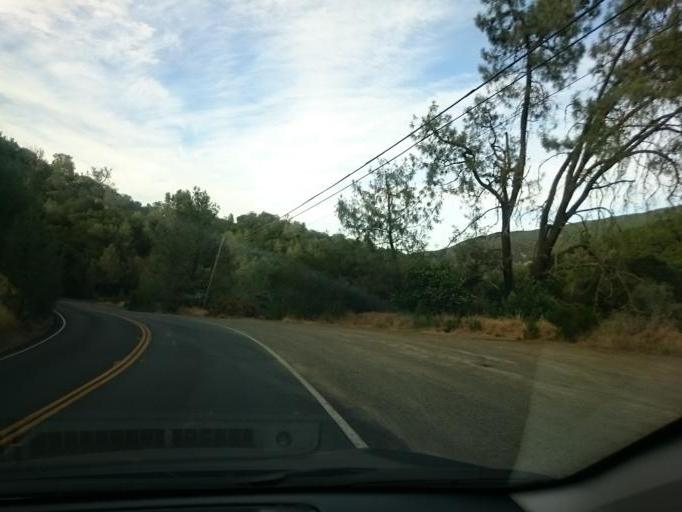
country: US
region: California
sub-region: Yolo County
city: Winters
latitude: 38.4759
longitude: -122.1414
